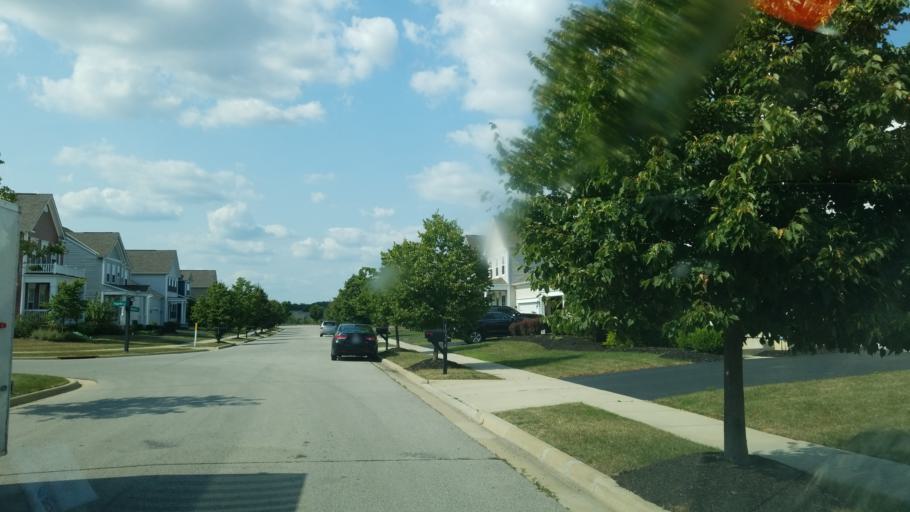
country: US
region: Ohio
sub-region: Union County
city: New California
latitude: 40.1646
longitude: -83.1883
